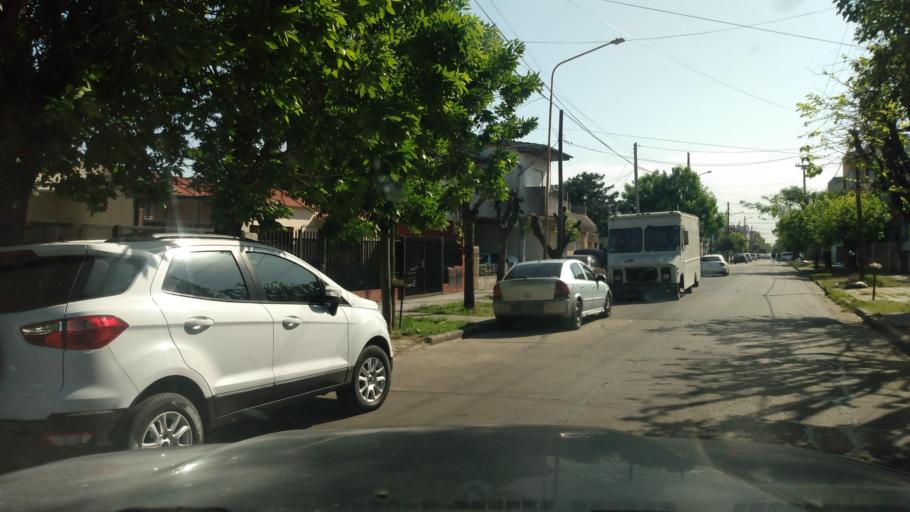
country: AR
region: Buenos Aires
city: San Justo
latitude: -34.6697
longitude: -58.5773
